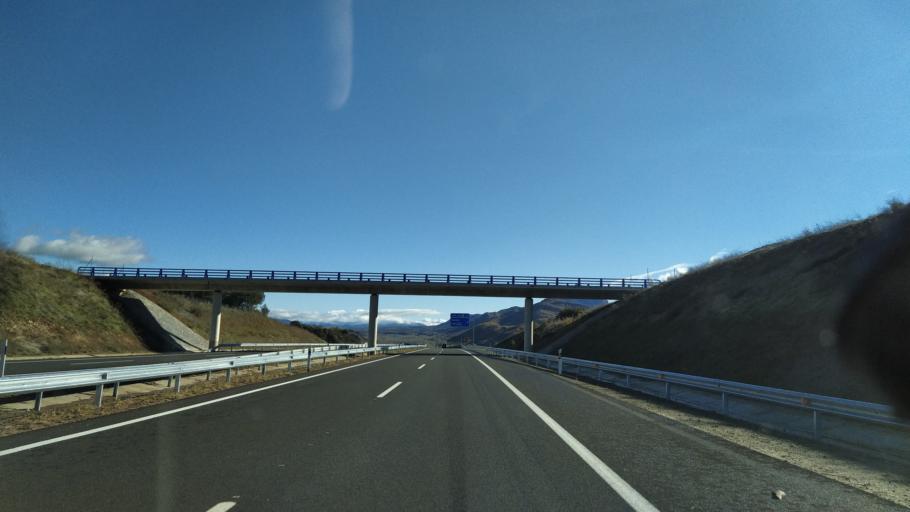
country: ES
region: Aragon
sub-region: Provincia de Huesca
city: Santa Cruz de la Seros
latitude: 42.5626
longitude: -0.6749
